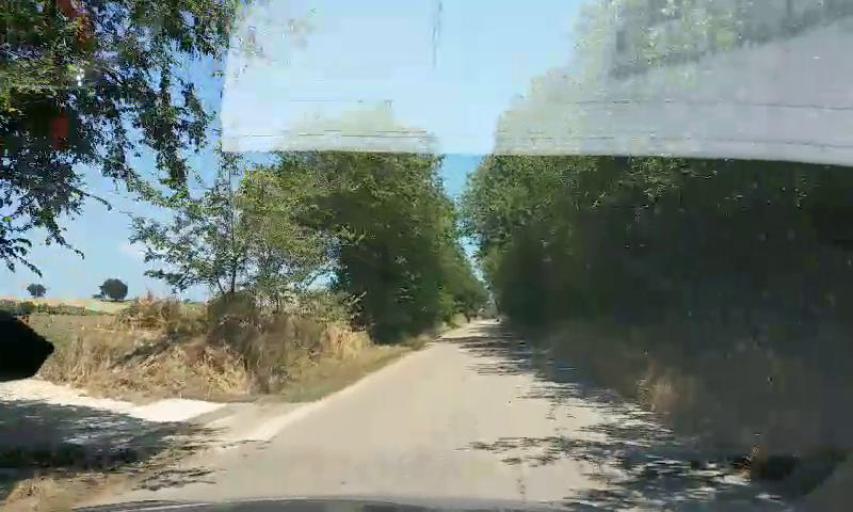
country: IT
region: Molise
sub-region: Provincia di Campobasso
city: Guglionesi
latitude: 41.9543
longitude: 14.9010
